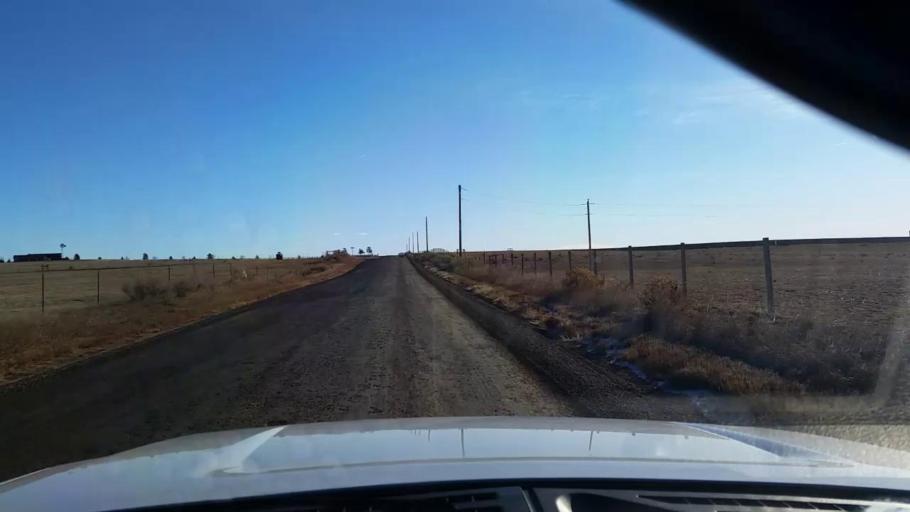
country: US
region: Colorado
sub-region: Larimer County
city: Wellington
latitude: 40.7696
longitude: -105.1118
